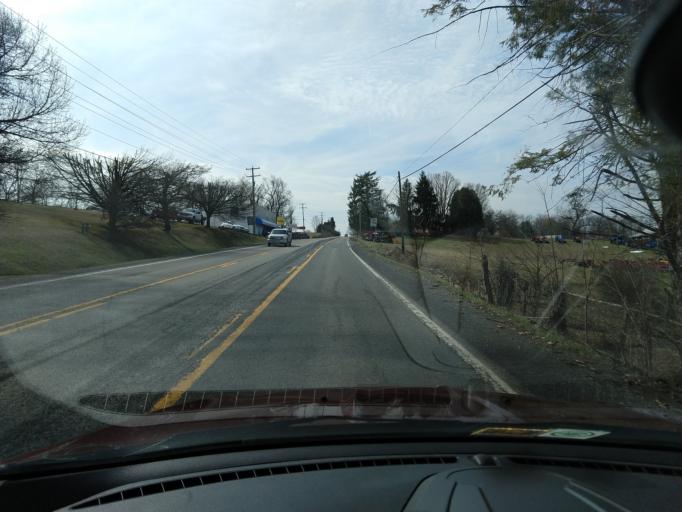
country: US
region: West Virginia
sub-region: Greenbrier County
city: Lewisburg
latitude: 37.8560
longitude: -80.4123
